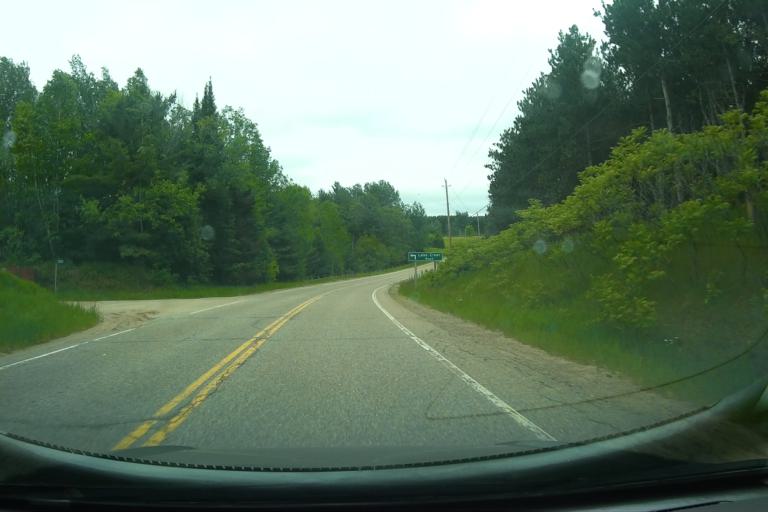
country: CA
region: Ontario
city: Pembroke
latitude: 45.4615
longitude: -77.2406
